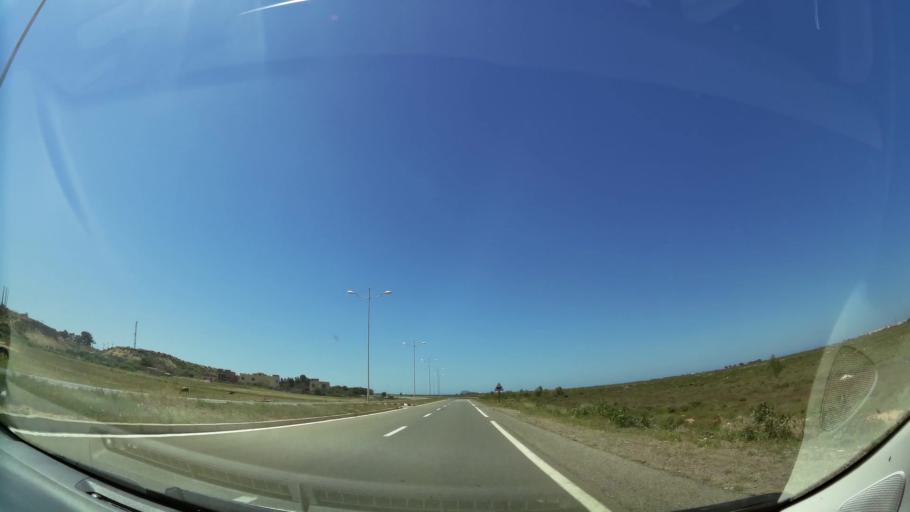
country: MA
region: Oriental
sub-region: Berkane-Taourirt
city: Madagh
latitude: 35.0981
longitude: -2.3210
